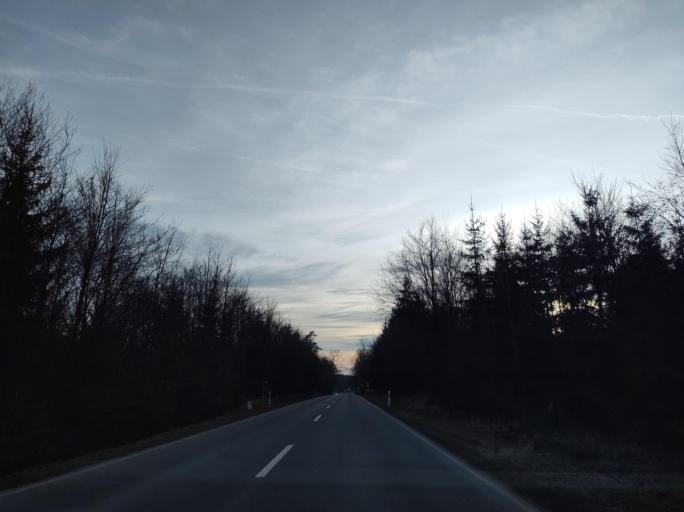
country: DE
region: North Rhine-Westphalia
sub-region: Regierungsbezirk Detmold
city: Schlangen
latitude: 51.8504
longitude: 8.8490
